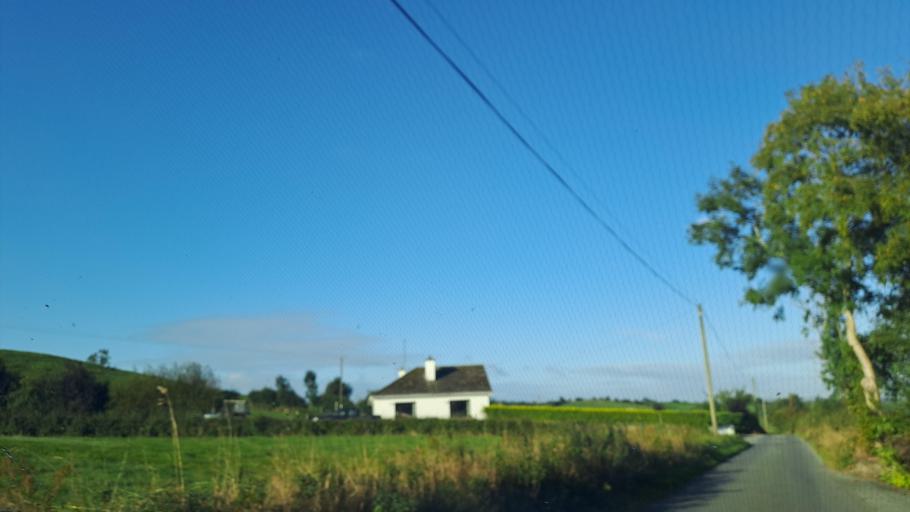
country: IE
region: Ulster
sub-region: An Cabhan
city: Kingscourt
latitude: 53.9885
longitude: -6.8580
